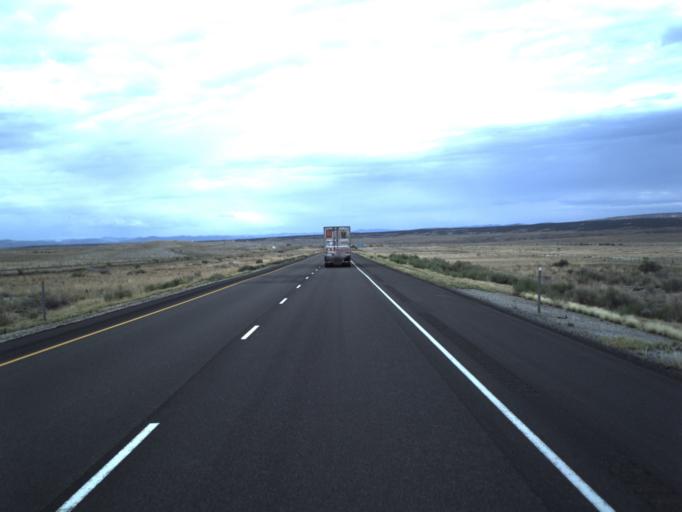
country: US
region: Colorado
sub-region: Mesa County
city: Loma
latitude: 39.0954
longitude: -109.2071
